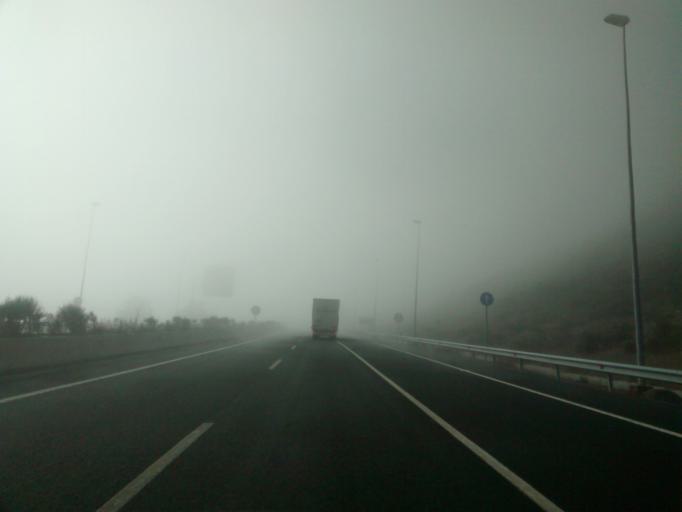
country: ES
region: Cantabria
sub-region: Provincia de Cantabria
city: Molledo
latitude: 43.1610
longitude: -4.0531
